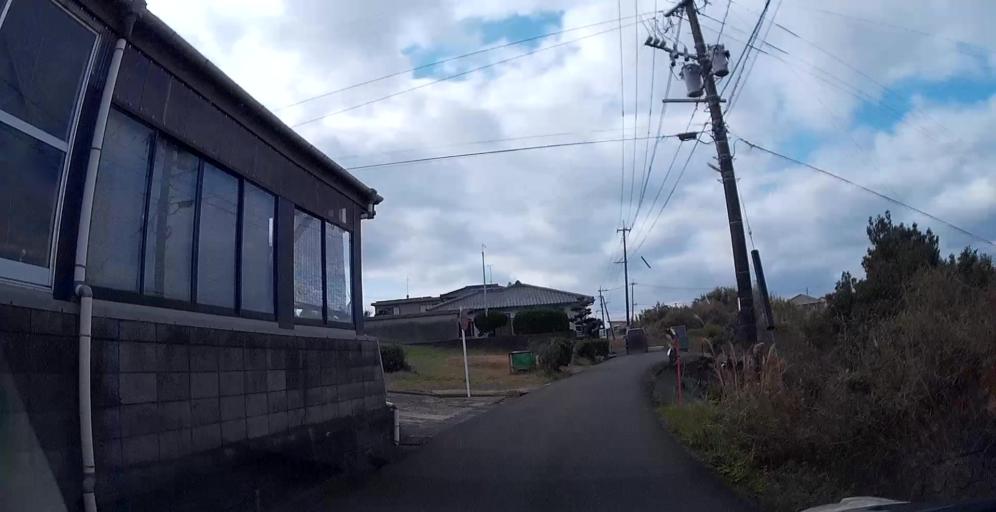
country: JP
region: Kumamoto
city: Minamata
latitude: 32.2058
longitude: 130.3849
